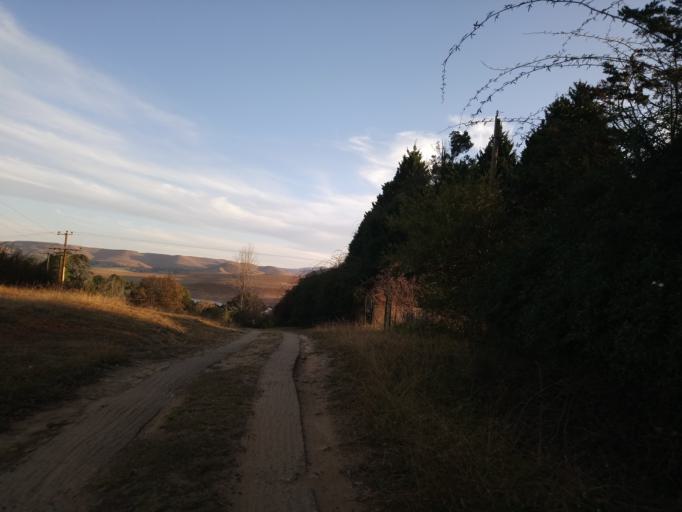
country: ZA
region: KwaZulu-Natal
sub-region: uMgungundlovu District Municipality
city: Mooirivier
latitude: -29.3305
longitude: 29.9195
